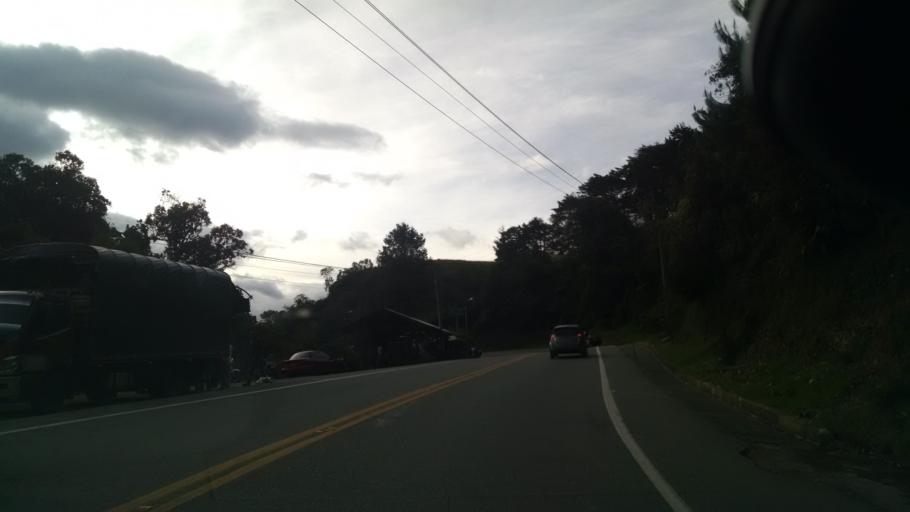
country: CO
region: Antioquia
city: Envigado
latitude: 6.1444
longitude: -75.5250
